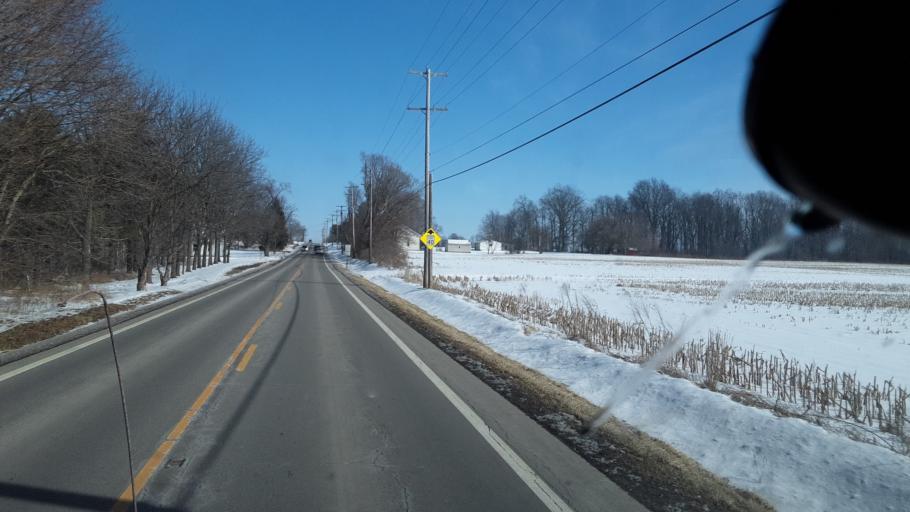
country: US
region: Ohio
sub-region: Columbiana County
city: Salem
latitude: 40.9441
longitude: -80.8014
